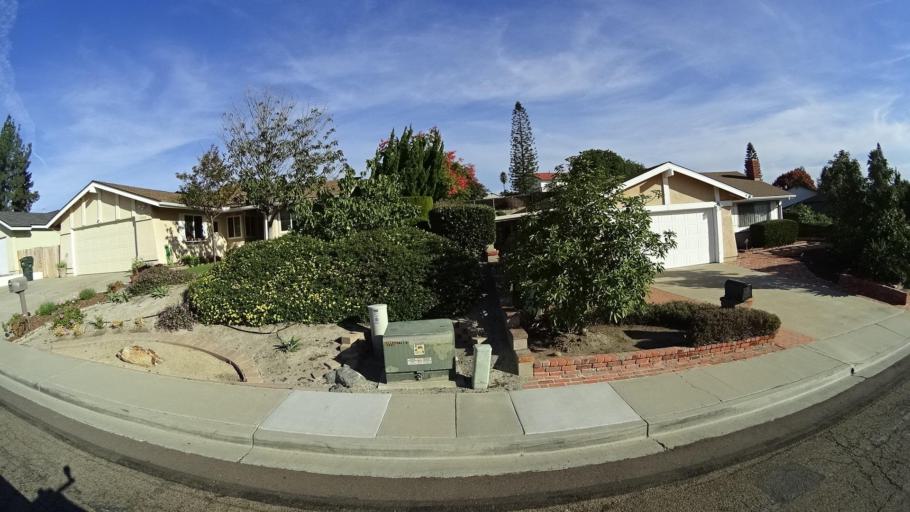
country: US
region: California
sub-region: San Diego County
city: Spring Valley
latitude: 32.7374
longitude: -116.9774
